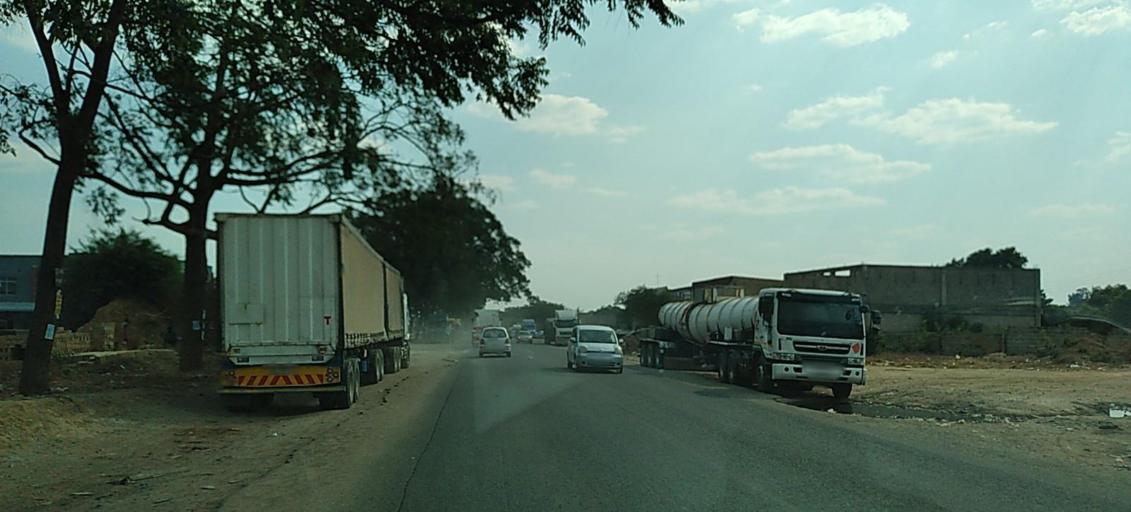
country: ZM
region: Copperbelt
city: Chililabombwe
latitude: -12.3700
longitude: 27.8519
